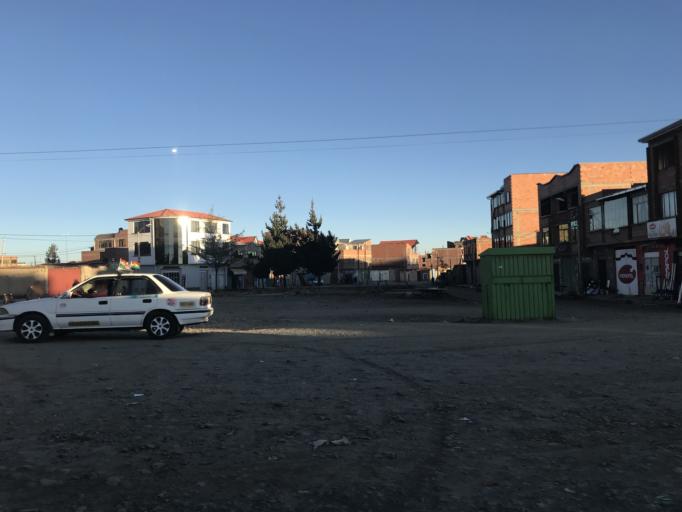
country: BO
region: La Paz
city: La Paz
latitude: -16.4989
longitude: -68.2320
